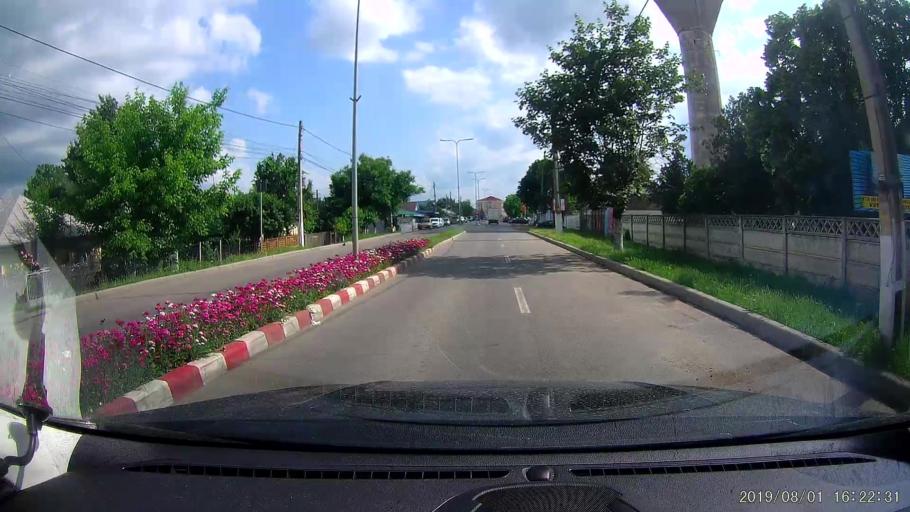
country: RO
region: Calarasi
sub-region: Municipiul Calarasi
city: Calarasi
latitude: 44.2036
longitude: 27.3375
